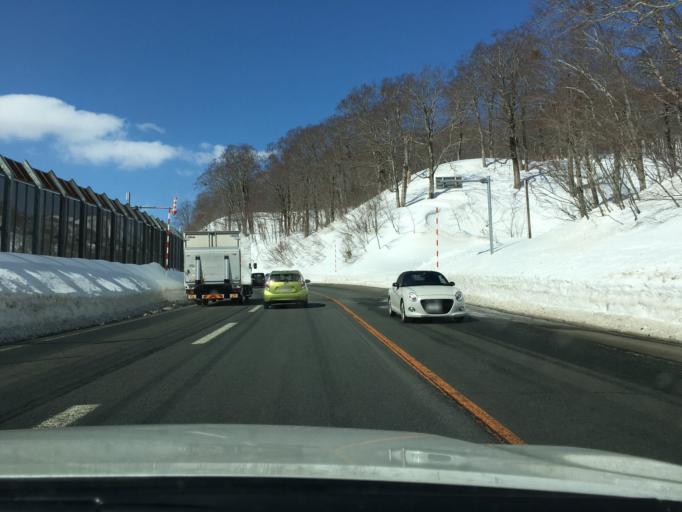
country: JP
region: Yamagata
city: Tsuruoka
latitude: 38.4949
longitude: 139.9723
